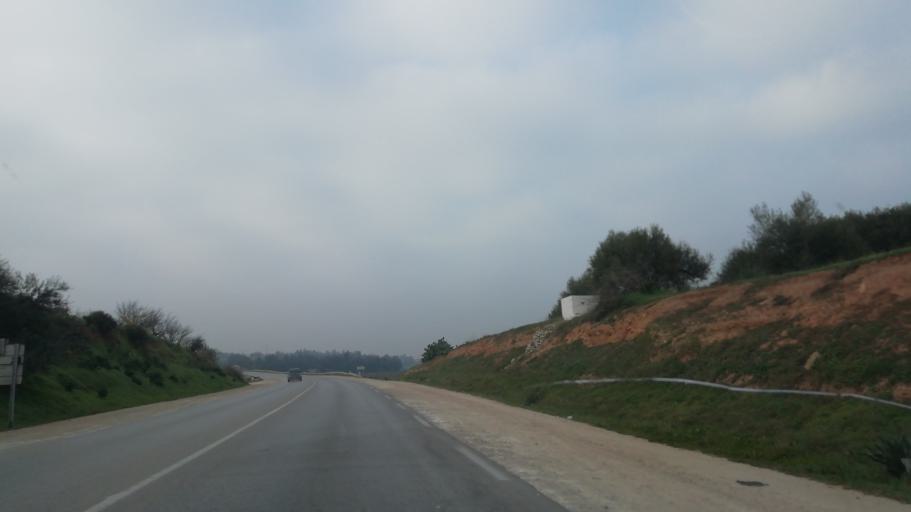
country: DZ
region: Relizane
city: Djidiouia
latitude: 35.9368
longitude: 0.8537
